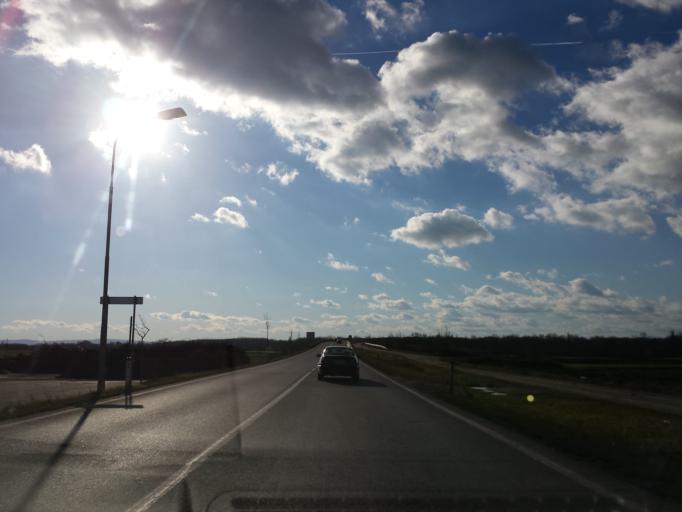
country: AT
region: Lower Austria
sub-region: Politischer Bezirk Wien-Umgebung
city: Himberg
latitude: 48.0704
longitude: 16.4585
